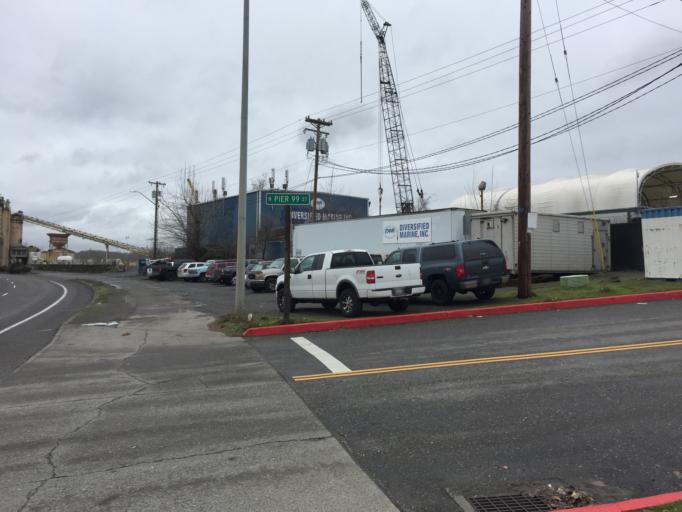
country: US
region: Washington
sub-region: Clark County
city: Vancouver
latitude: 45.6069
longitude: -122.6848
